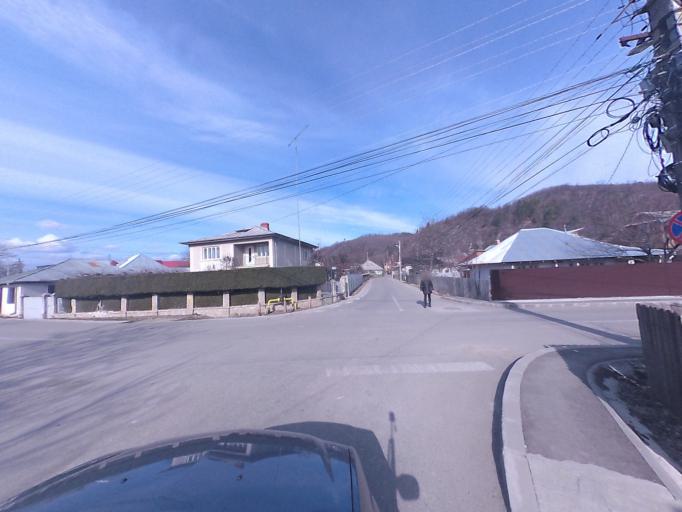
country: RO
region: Neamt
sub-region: Oras Targu Neamt
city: Humulesti
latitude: 47.2061
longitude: 26.3548
